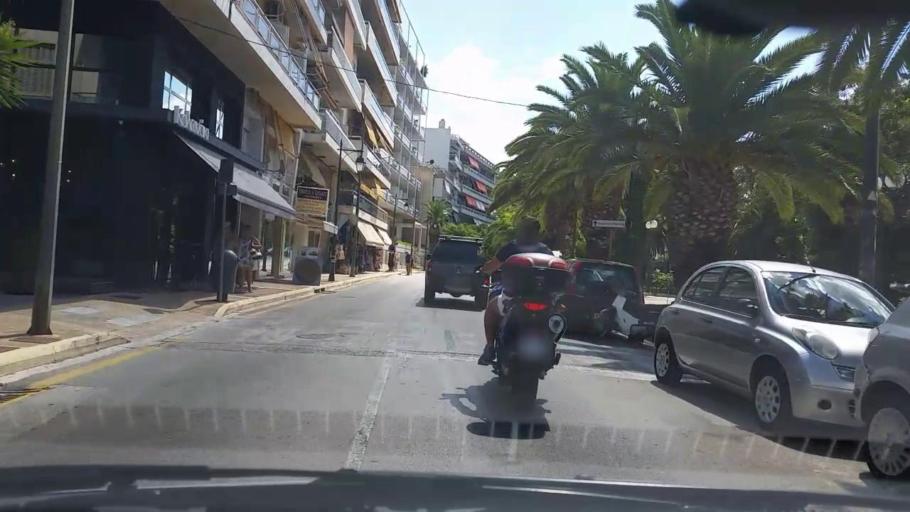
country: GR
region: Peloponnese
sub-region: Nomos Korinthias
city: Loutraki
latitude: 37.9798
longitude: 22.9758
